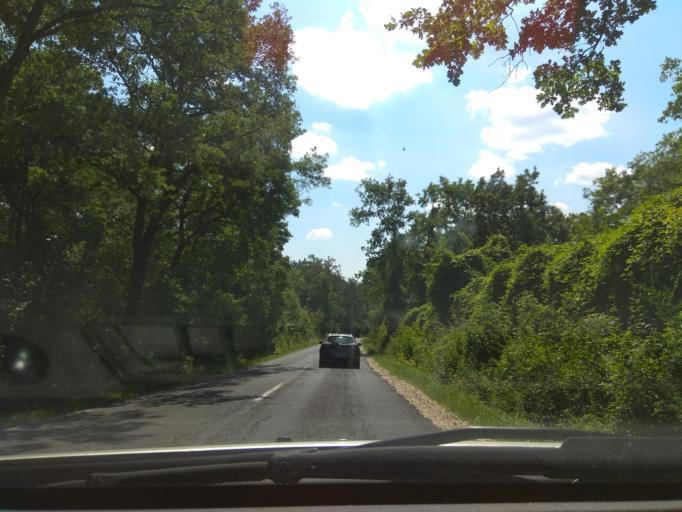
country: HU
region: Borsod-Abauj-Zemplen
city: Harsany
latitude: 48.0190
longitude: 20.7638
